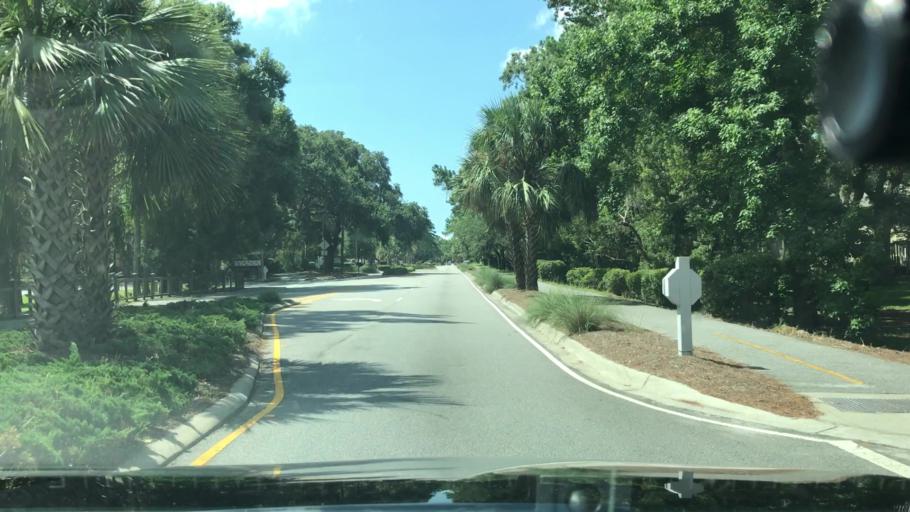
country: US
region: South Carolina
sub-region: Beaufort County
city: Hilton Head Island
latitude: 32.2114
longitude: -80.7027
